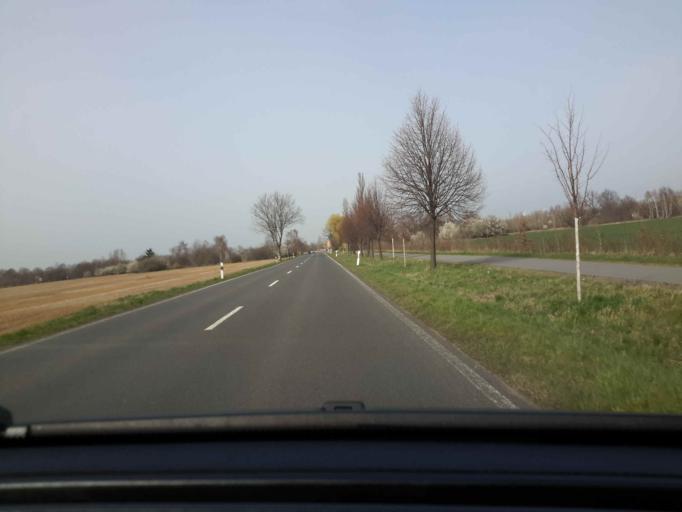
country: DE
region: Saxony
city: Rackwitz
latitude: 51.4298
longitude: 12.3549
